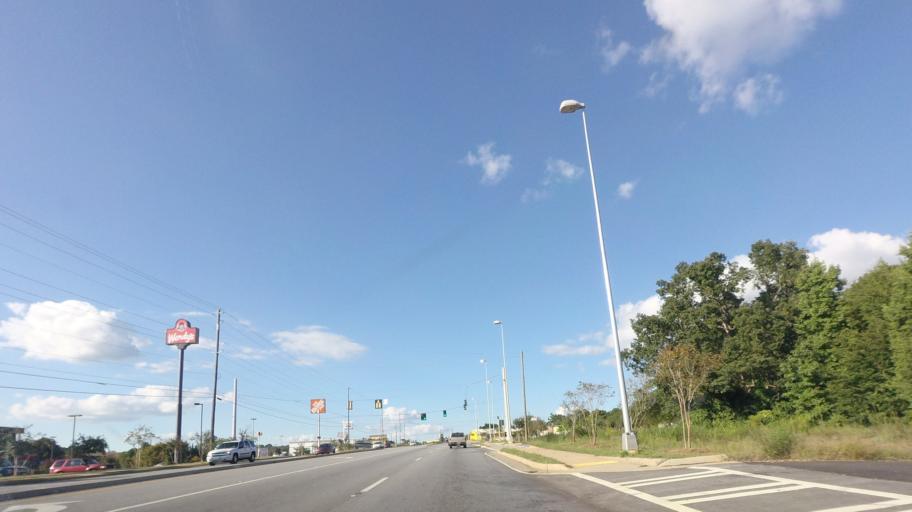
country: US
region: Georgia
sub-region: Upson County
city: Hannahs Mill
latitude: 32.9211
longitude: -84.3338
